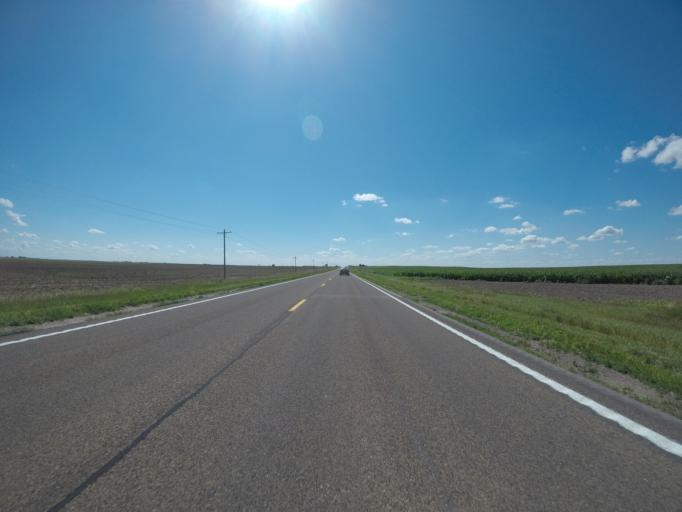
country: US
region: Nebraska
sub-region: Chase County
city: Imperial
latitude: 40.5375
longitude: -101.8207
